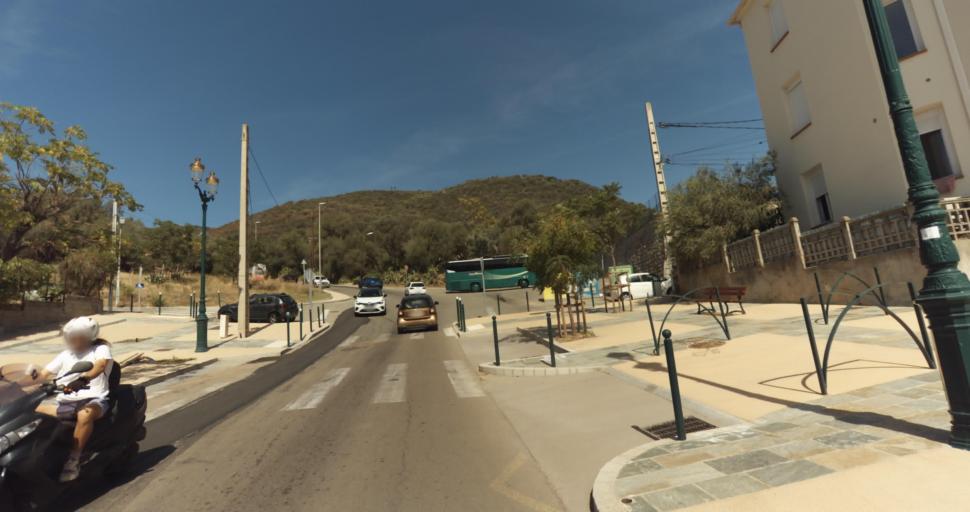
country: FR
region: Corsica
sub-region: Departement de la Corse-du-Sud
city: Ajaccio
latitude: 41.9154
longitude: 8.7242
